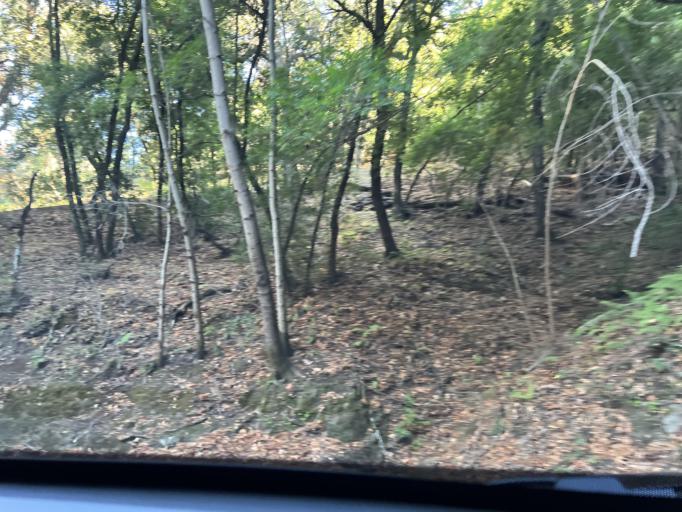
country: US
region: California
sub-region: Santa Clara County
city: Loyola
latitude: 37.2945
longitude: -122.1125
